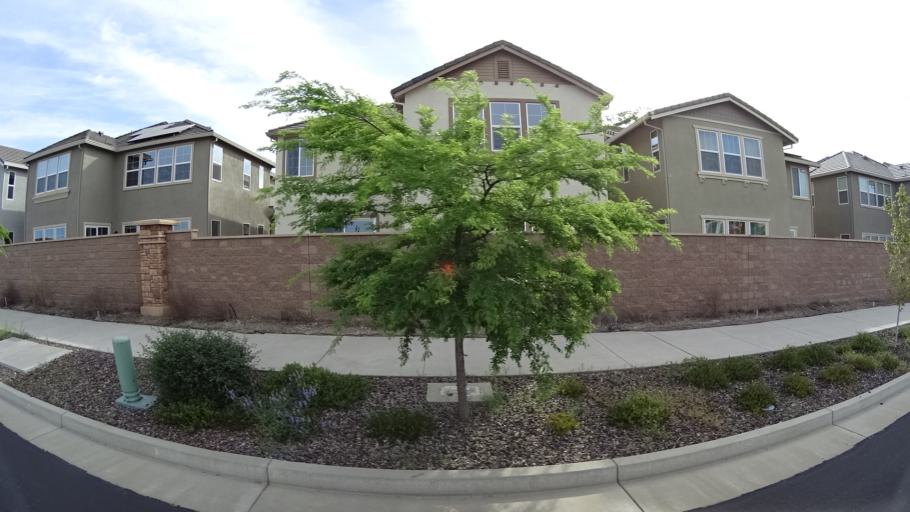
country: US
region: California
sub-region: Placer County
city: Lincoln
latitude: 38.8257
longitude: -121.2939
